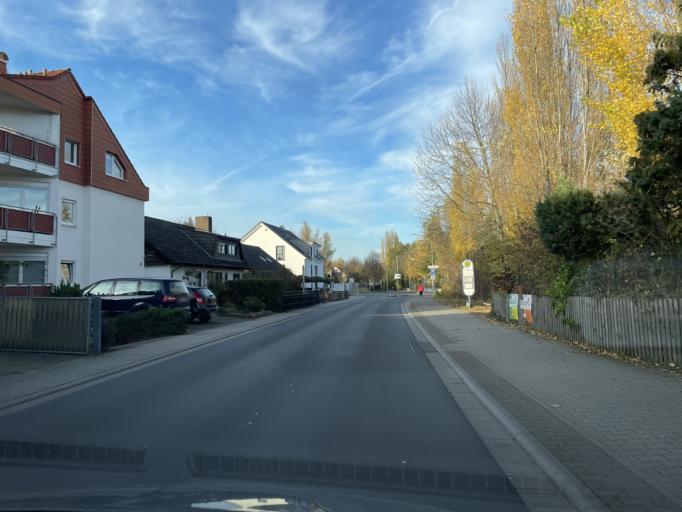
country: DE
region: Hesse
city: Gross-Umstadt
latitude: 49.8726
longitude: 8.9267
